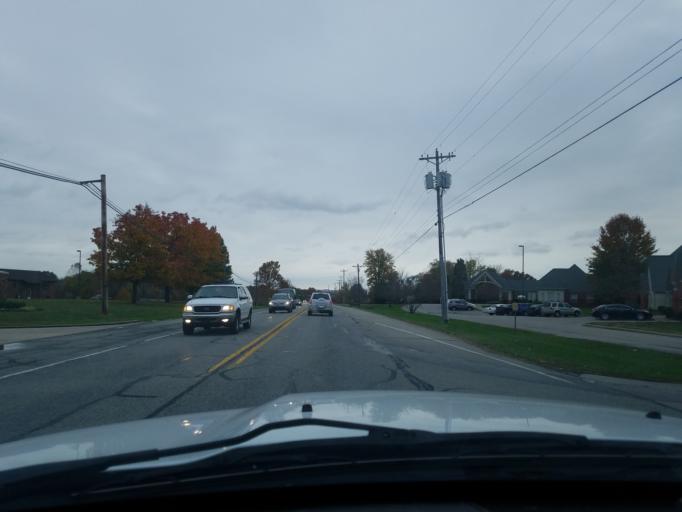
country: US
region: Indiana
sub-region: Clark County
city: Sellersburg
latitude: 38.3612
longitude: -85.7835
